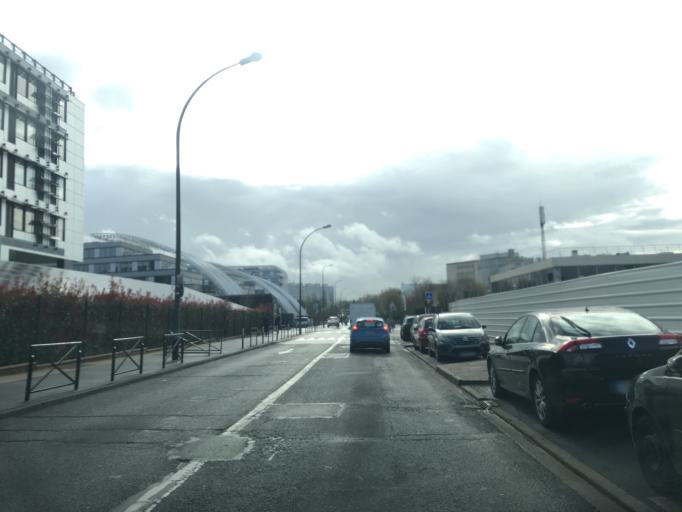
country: FR
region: Ile-de-France
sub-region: Departement des Yvelines
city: Velizy-Villacoublay
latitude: 48.7878
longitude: 2.2170
